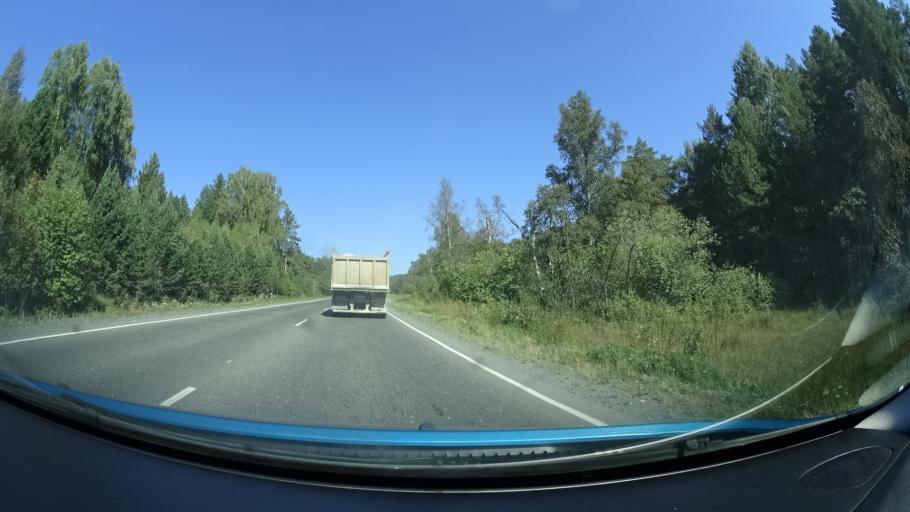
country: RU
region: Bashkortostan
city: Abzakovo
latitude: 53.8684
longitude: 58.5389
